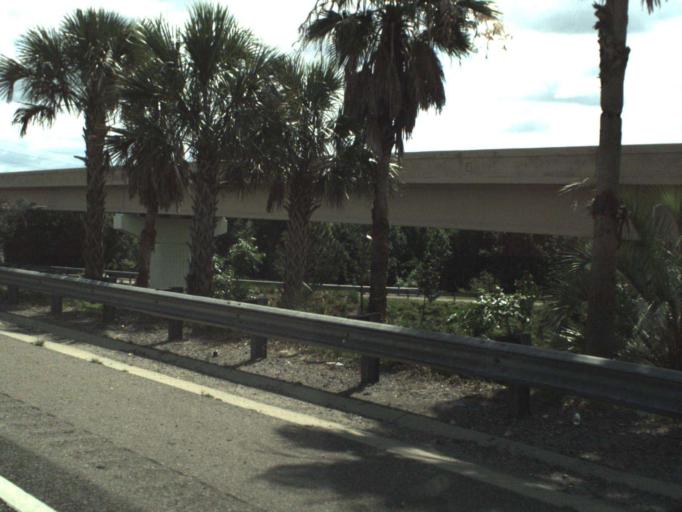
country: US
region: Florida
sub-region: Volusia County
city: DeBary
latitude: 28.8304
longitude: -81.3239
